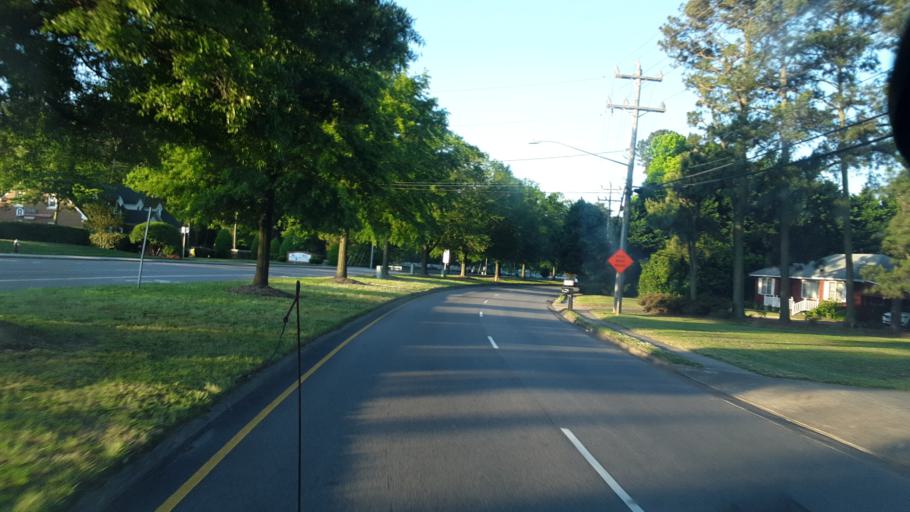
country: US
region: Virginia
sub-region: City of Virginia Beach
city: Virginia Beach
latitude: 36.7632
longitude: -76.0158
